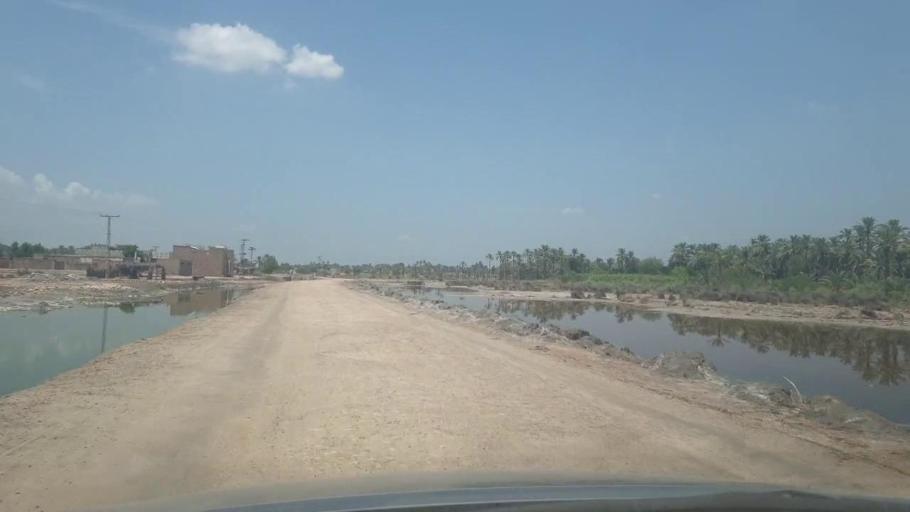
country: PK
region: Sindh
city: Kot Diji
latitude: 27.4140
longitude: 68.7372
